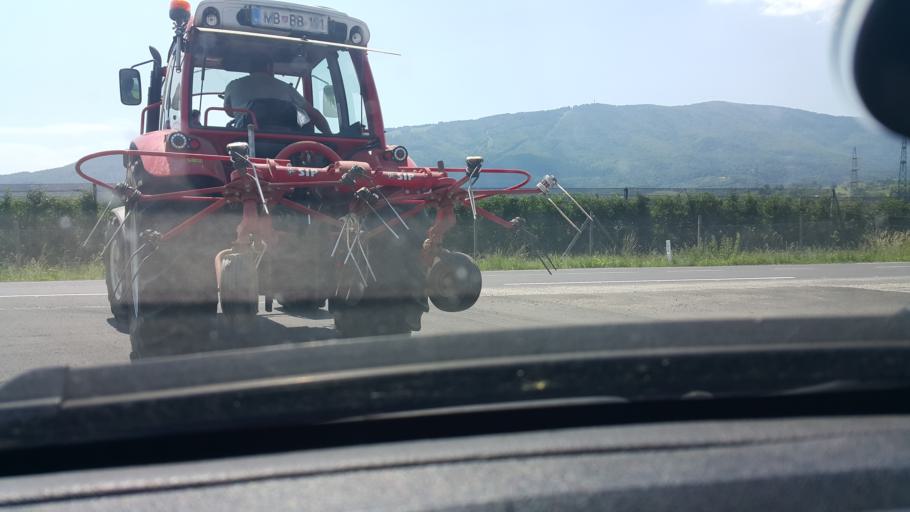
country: SI
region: Maribor
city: Pekre
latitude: 46.5580
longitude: 15.5965
